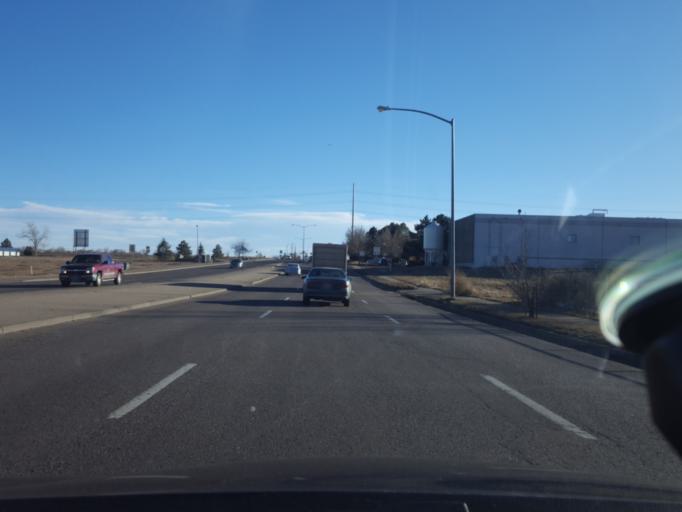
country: US
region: Colorado
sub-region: Adams County
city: Aurora
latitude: 39.7578
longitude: -104.7723
